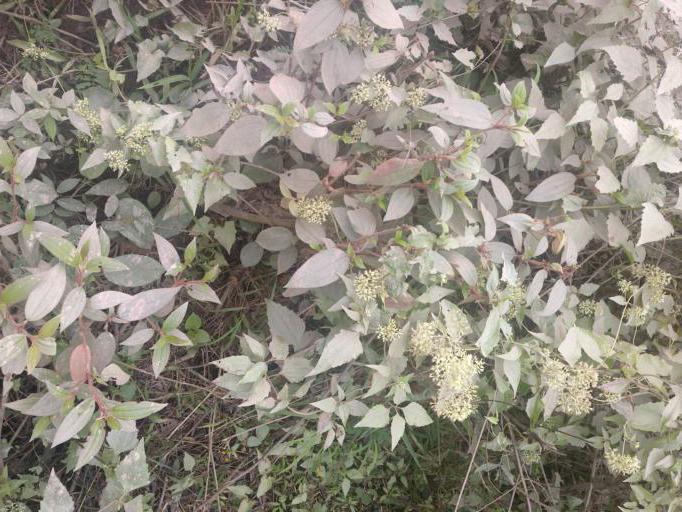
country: LA
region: Xiangkhoang
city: Muang Phonsavan
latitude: 19.3336
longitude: 103.6477
